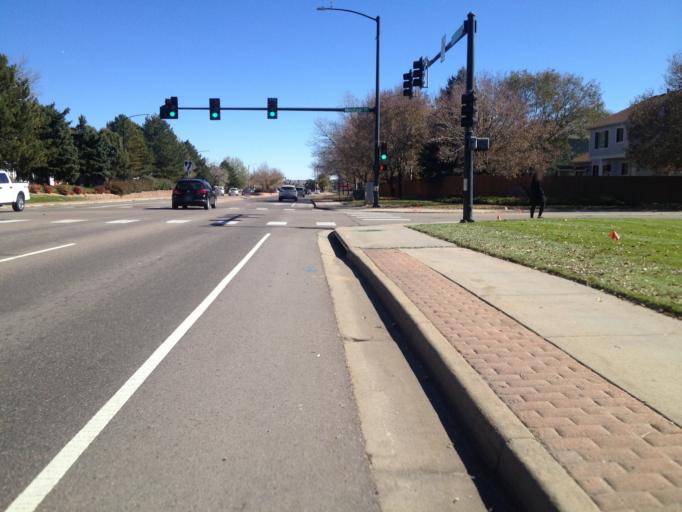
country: US
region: Colorado
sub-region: Boulder County
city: Lafayette
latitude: 39.9868
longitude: -105.1019
